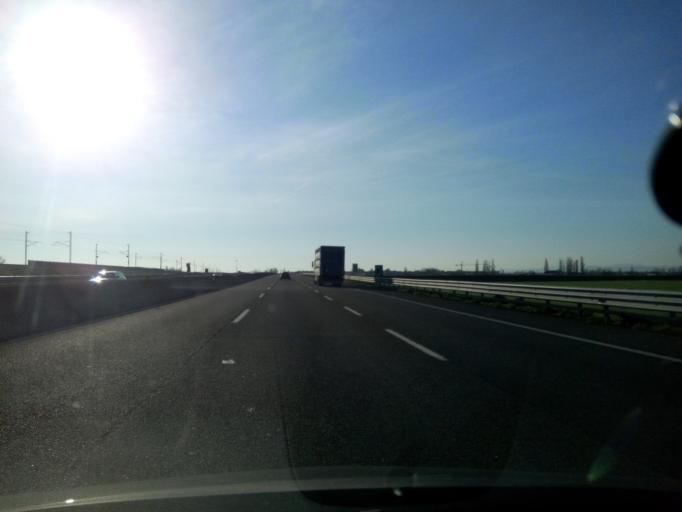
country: IT
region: Emilia-Romagna
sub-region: Provincia di Reggio Emilia
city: Roncocesi
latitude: 44.7469
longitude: 10.5641
